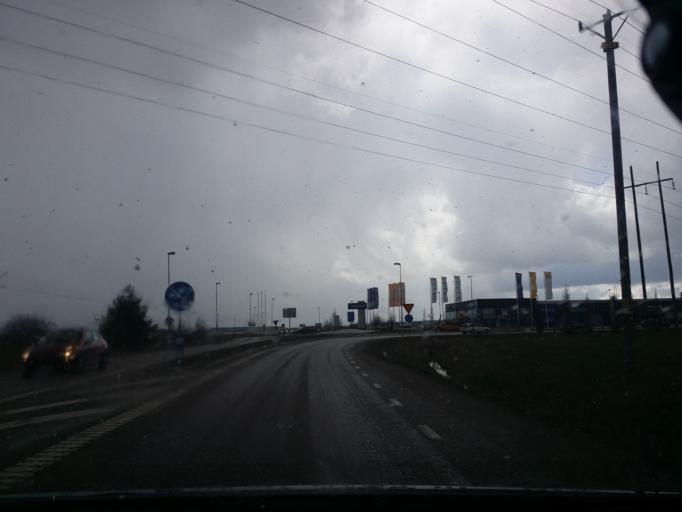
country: SE
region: Vaestmanland
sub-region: Sala Kommun
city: Sala
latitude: 59.9113
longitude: 16.6192
